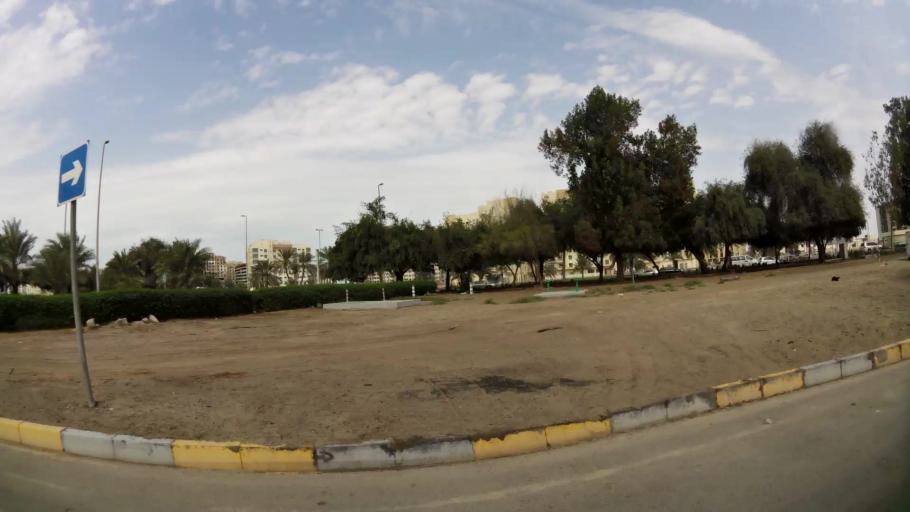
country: AE
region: Abu Dhabi
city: Abu Dhabi
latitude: 24.4162
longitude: 54.4654
